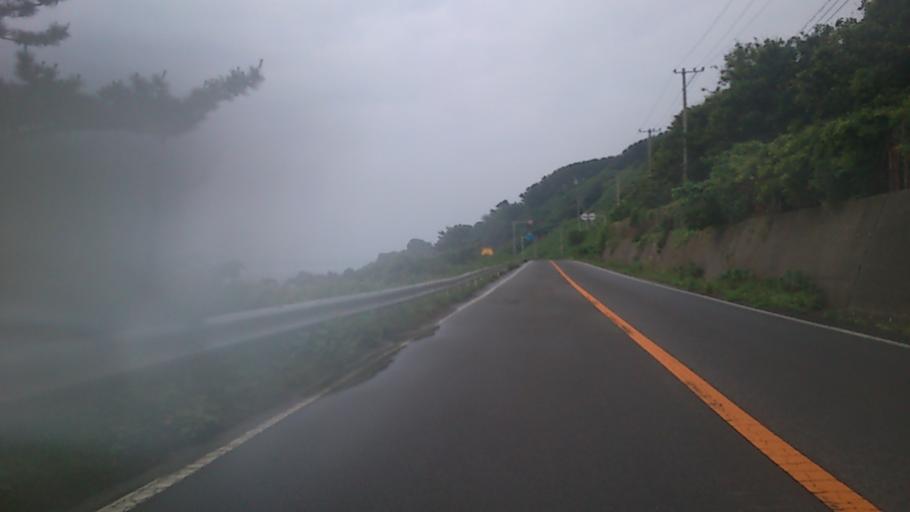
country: JP
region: Akita
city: Noshiromachi
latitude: 40.4403
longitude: 139.9402
